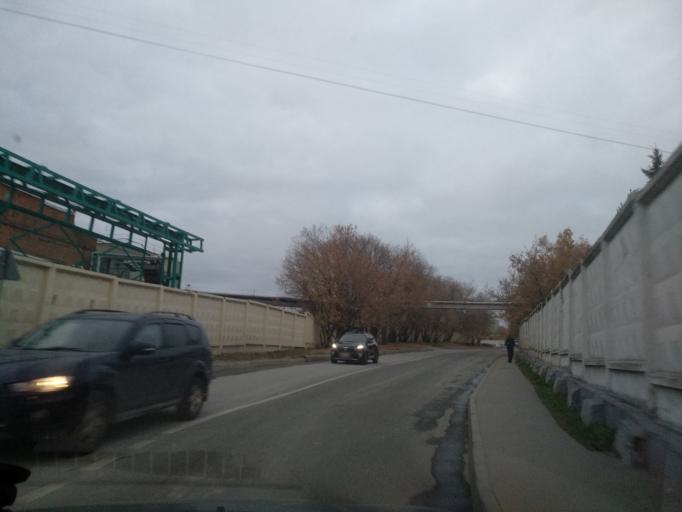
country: RU
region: Moscow
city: Kozeyevo
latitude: 55.8804
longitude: 37.6289
